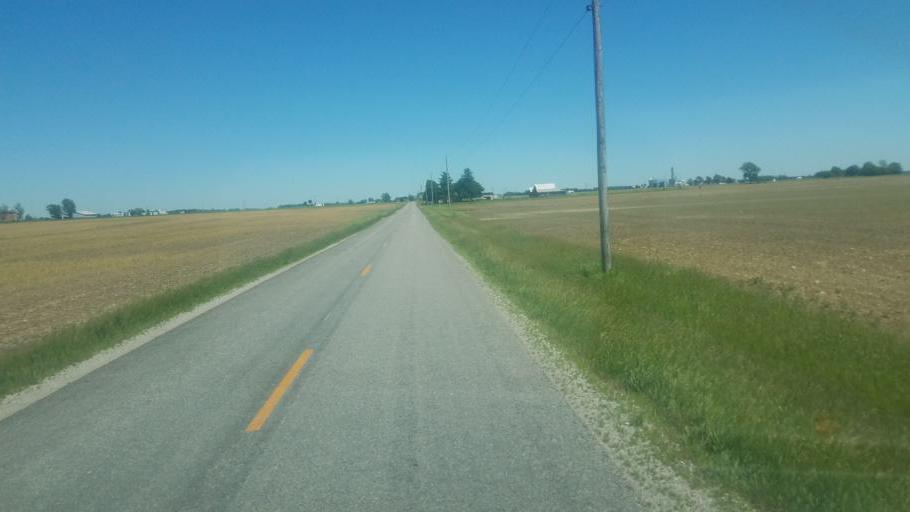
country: US
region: Ohio
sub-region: Shelby County
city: Sidney
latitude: 40.2115
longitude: -84.1215
